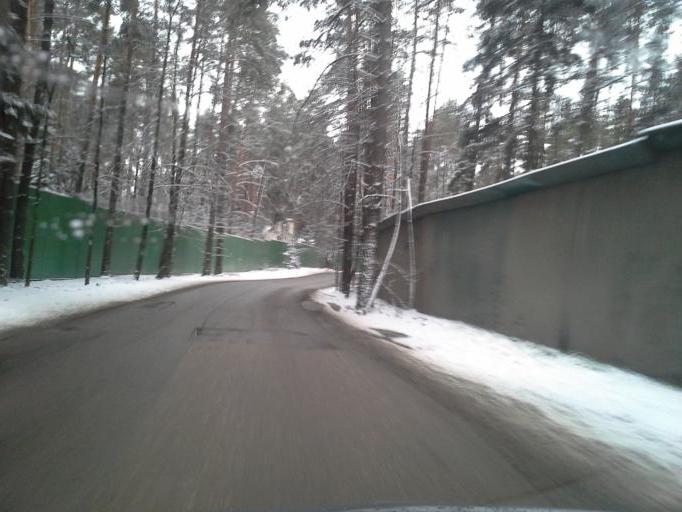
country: RU
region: Moskovskaya
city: Nikolina Gora
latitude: 55.7387
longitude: 37.0444
